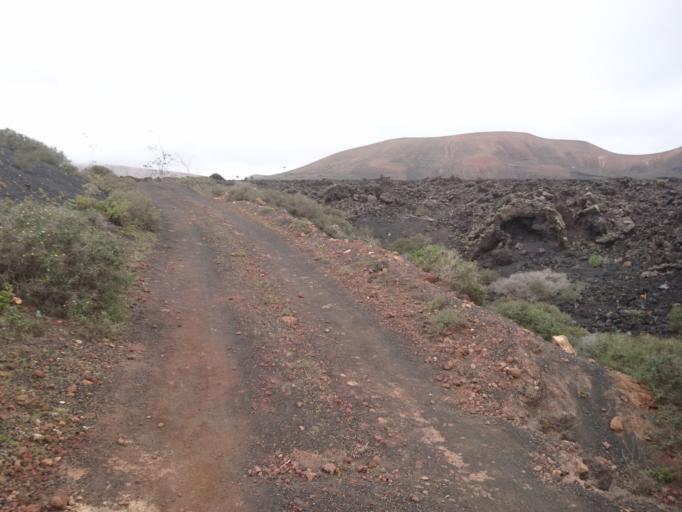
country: ES
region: Canary Islands
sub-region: Provincia de Las Palmas
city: Tinajo
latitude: 29.0169
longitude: -13.6940
